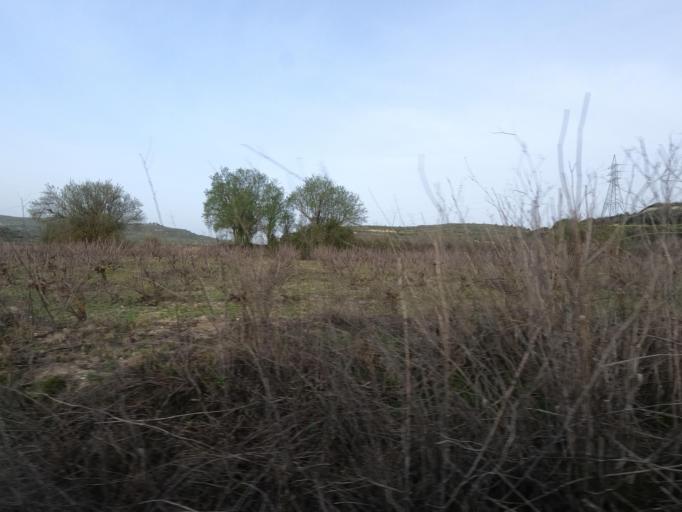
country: CY
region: Pafos
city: Mesogi
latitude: 34.8724
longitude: 32.4928
